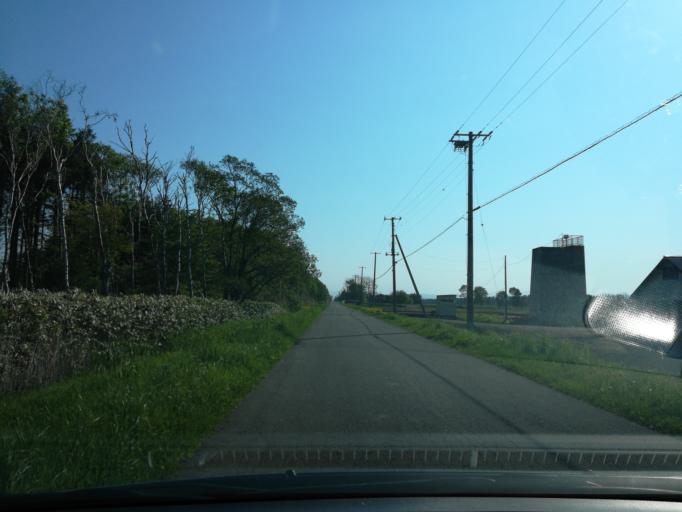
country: JP
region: Hokkaido
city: Ebetsu
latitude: 43.1149
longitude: 141.6449
